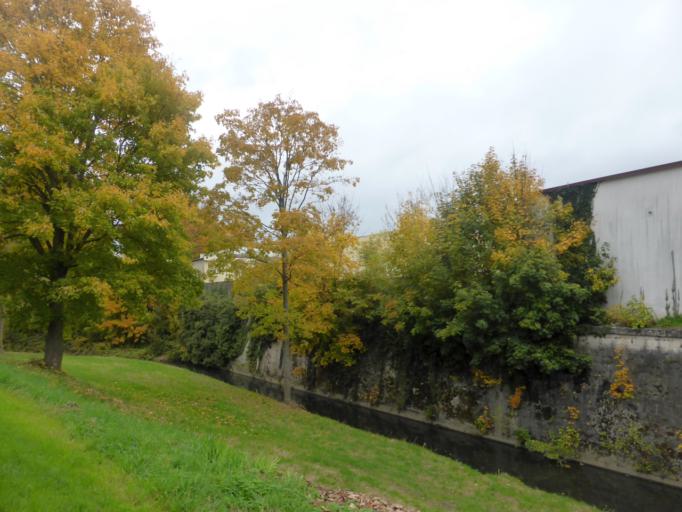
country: FR
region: Lorraine
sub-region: Departement de Meurthe-et-Moselle
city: Toul
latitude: 48.6720
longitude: 5.8874
